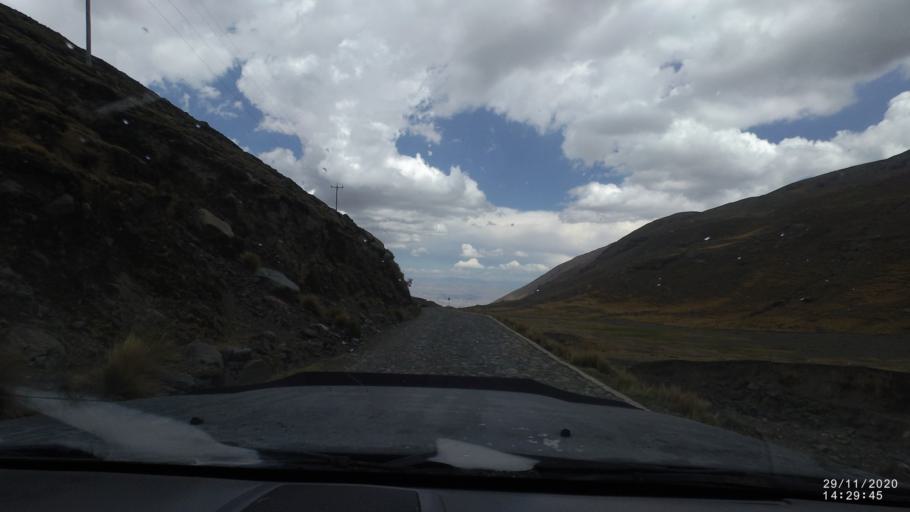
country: BO
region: Cochabamba
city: Sipe Sipe
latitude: -17.2622
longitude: -66.3533
